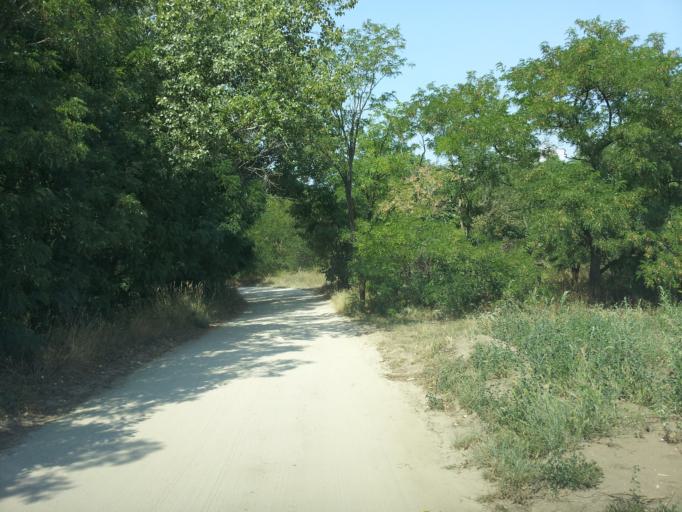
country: HU
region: Pest
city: Dunavarsany
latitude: 47.2648
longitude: 19.0650
